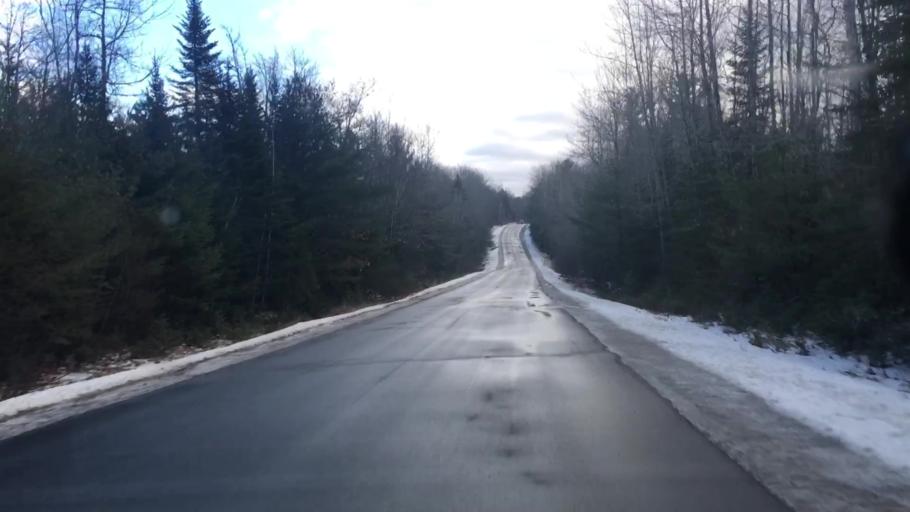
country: US
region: Maine
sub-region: Hancock County
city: Dedham
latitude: 44.6886
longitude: -68.7151
